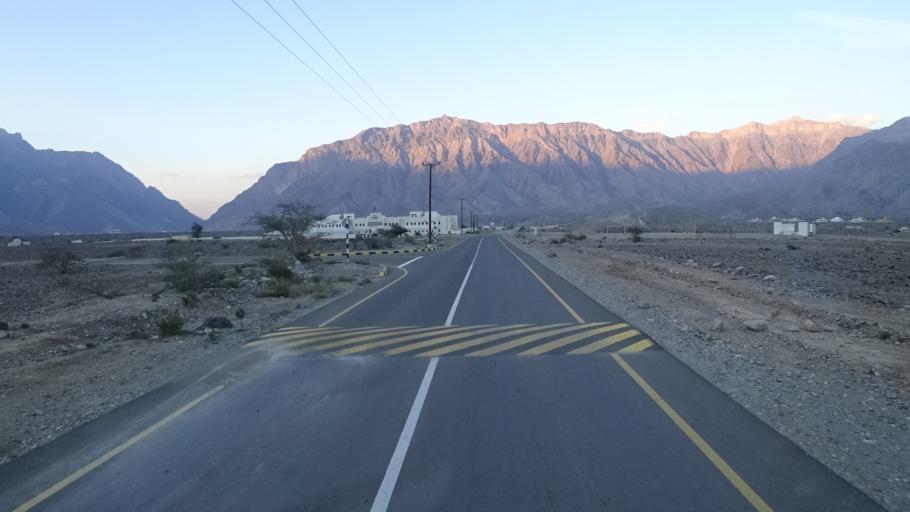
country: OM
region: Al Batinah
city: Rustaq
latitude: 23.2768
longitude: 57.3268
